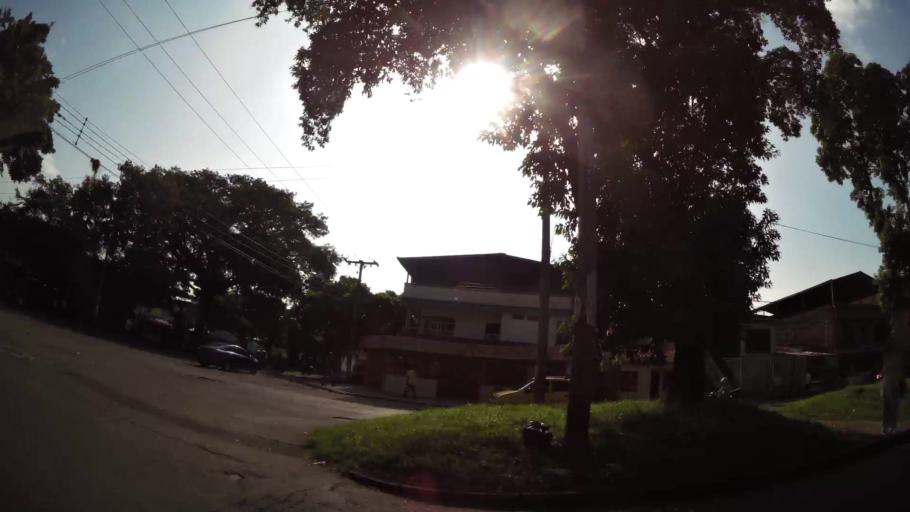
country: CO
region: Valle del Cauca
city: Cali
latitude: 3.4148
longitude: -76.5284
